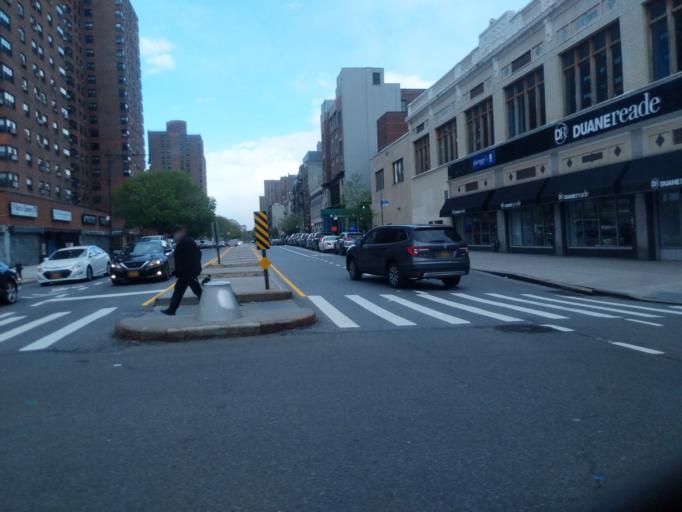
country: US
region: New York
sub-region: New York County
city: Manhattan
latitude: 40.7914
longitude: -73.9447
